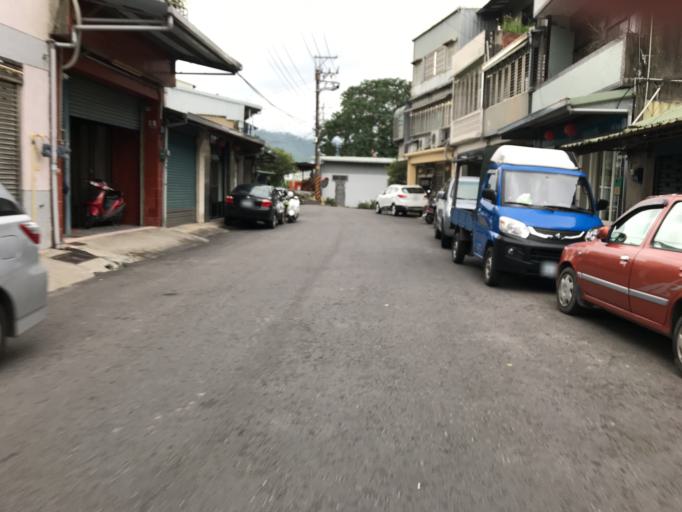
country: TW
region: Taiwan
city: Daxi
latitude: 24.7872
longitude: 121.1766
